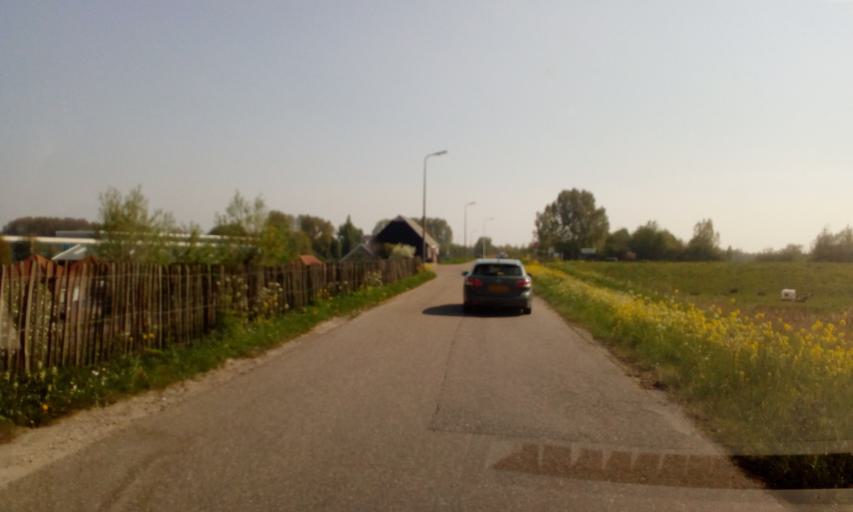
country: NL
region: South Holland
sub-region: Gemeente Zwijndrecht
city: Heerjansdam
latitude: 51.8123
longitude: 4.5889
